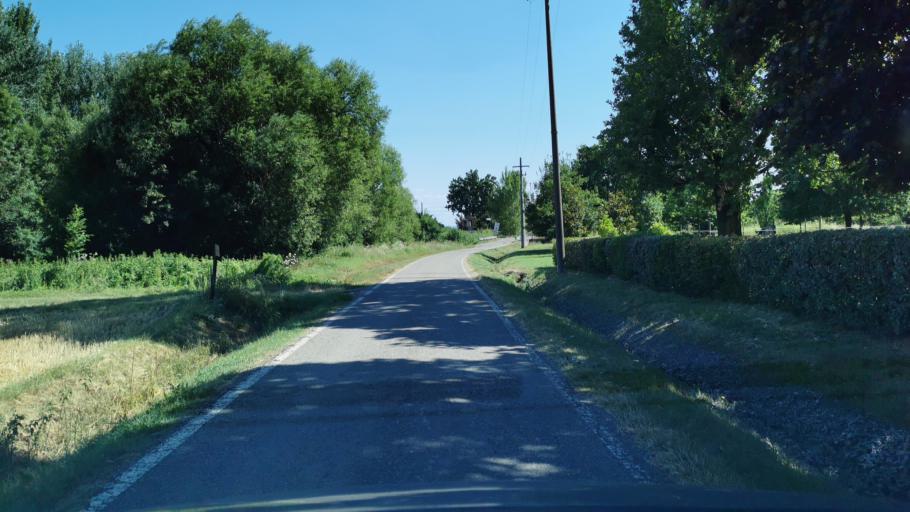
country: IT
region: Emilia-Romagna
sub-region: Provincia di Modena
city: Villanova
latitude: 44.6945
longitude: 10.9074
